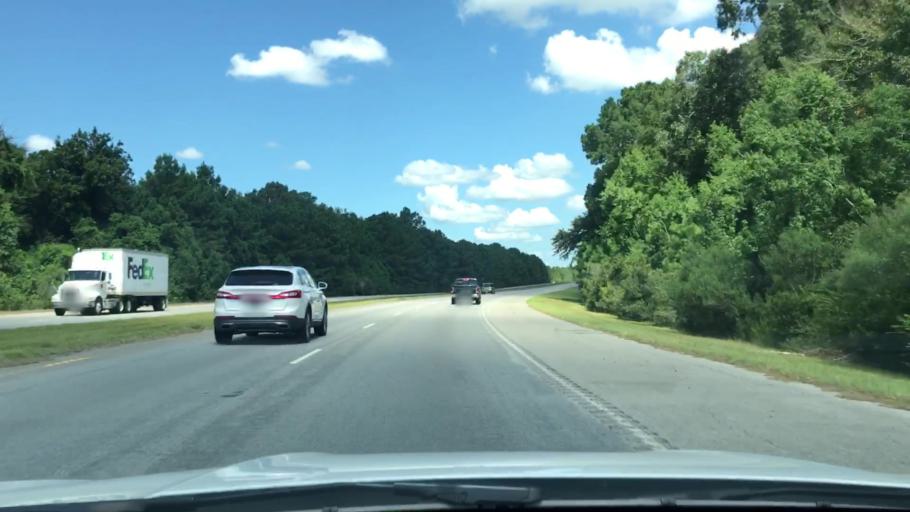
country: US
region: South Carolina
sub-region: Berkeley County
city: Hanahan
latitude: 32.9265
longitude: -79.9957
